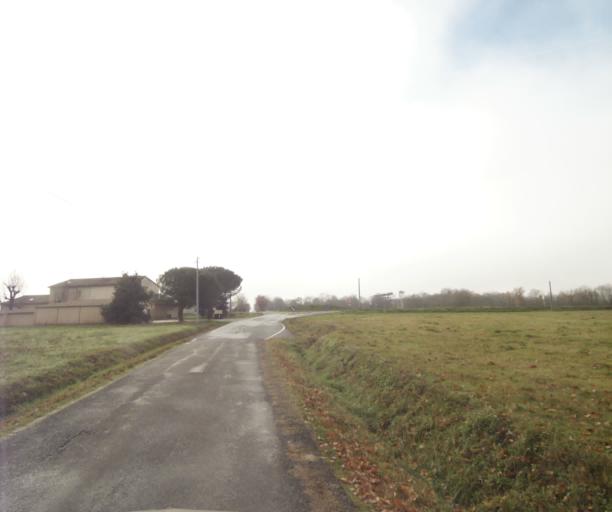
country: FR
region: Midi-Pyrenees
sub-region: Departement de la Haute-Garonne
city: Villemur-sur-Tarn
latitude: 43.8522
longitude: 1.4898
